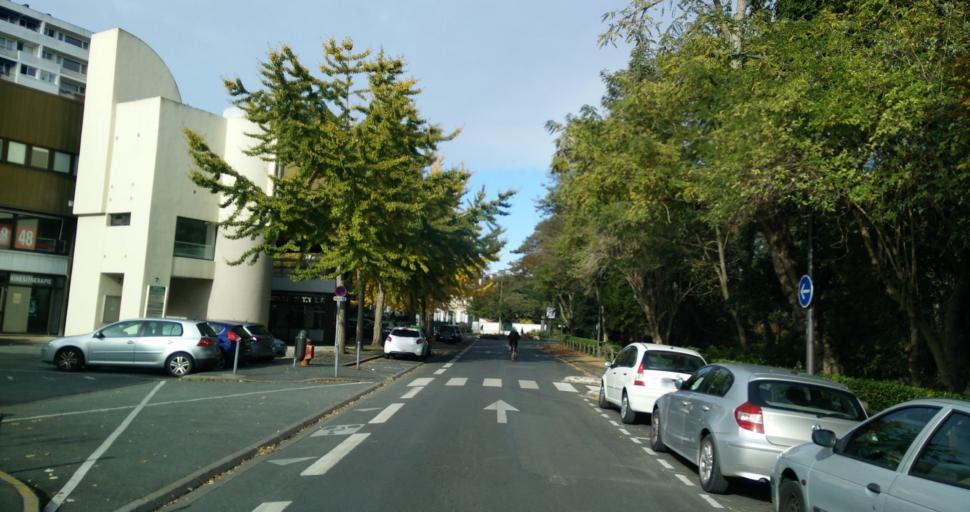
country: FR
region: Poitou-Charentes
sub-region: Departement de la Charente-Maritime
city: La Rochelle
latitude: 46.1614
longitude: -1.1583
